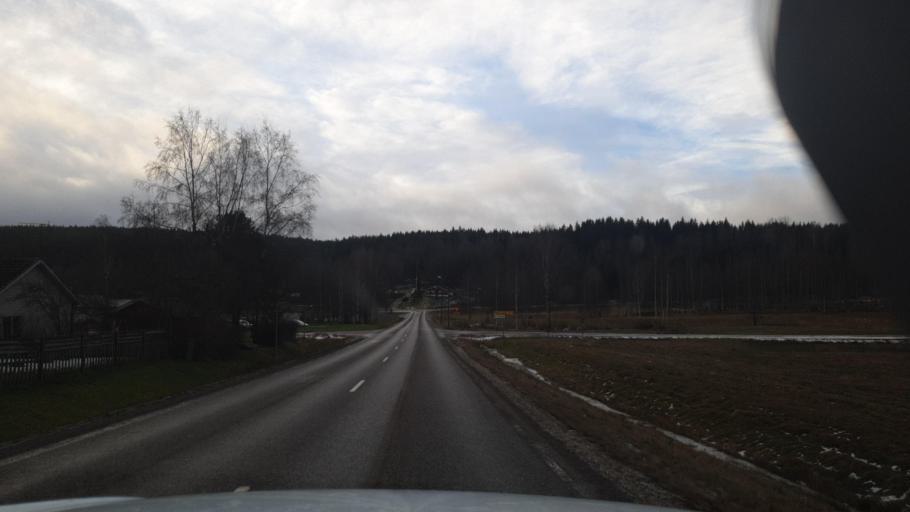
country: SE
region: Vaermland
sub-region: Eda Kommun
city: Amotfors
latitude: 59.6815
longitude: 12.4115
